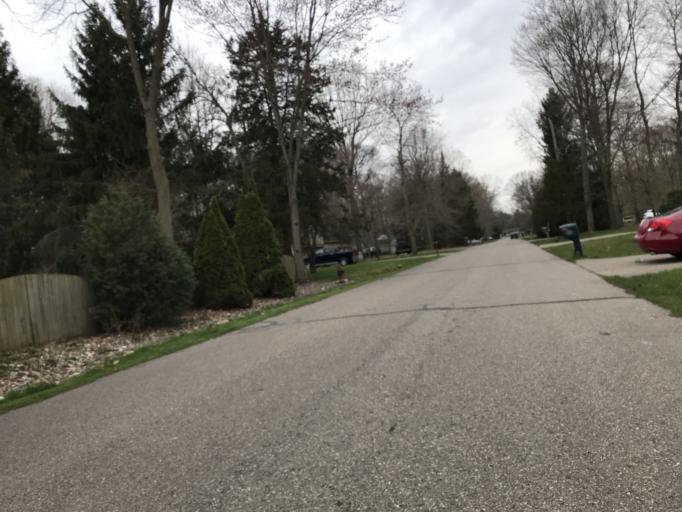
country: US
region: Michigan
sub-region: Oakland County
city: Farmington
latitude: 42.4644
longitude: -83.3386
